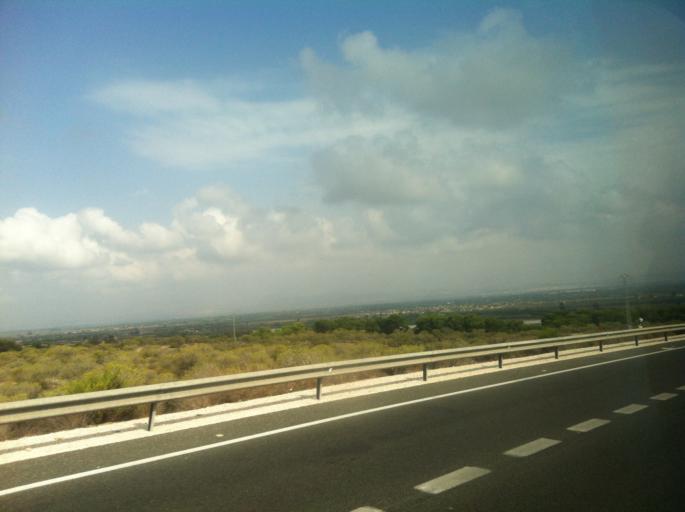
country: ES
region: Valencia
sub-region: Provincia de Alicante
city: Guardamar del Segura
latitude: 38.1534
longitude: -0.6574
